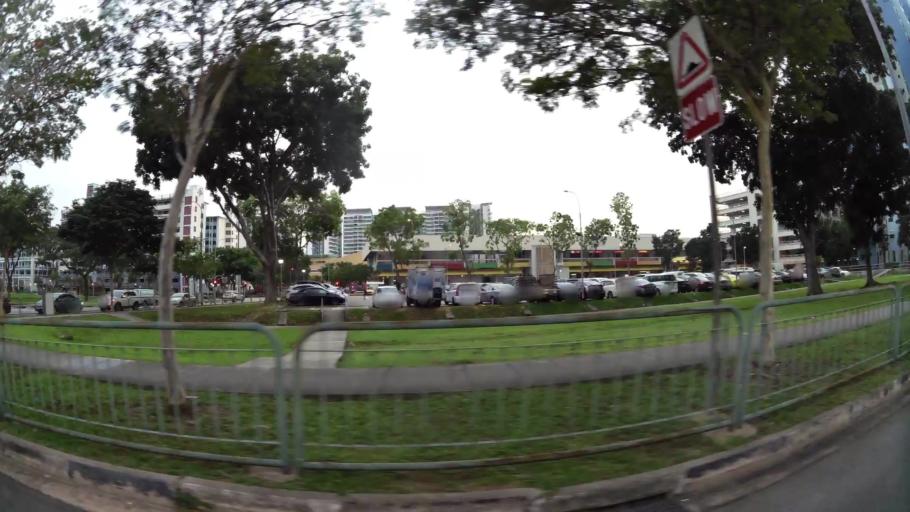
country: SG
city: Singapore
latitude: 1.3094
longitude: 103.8861
